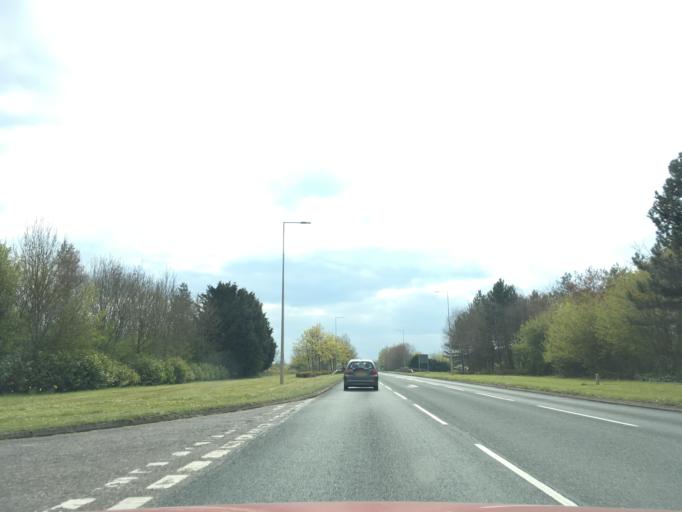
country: GB
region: England
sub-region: Milton Keynes
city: Shenley Church End
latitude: 52.0101
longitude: -0.7806
